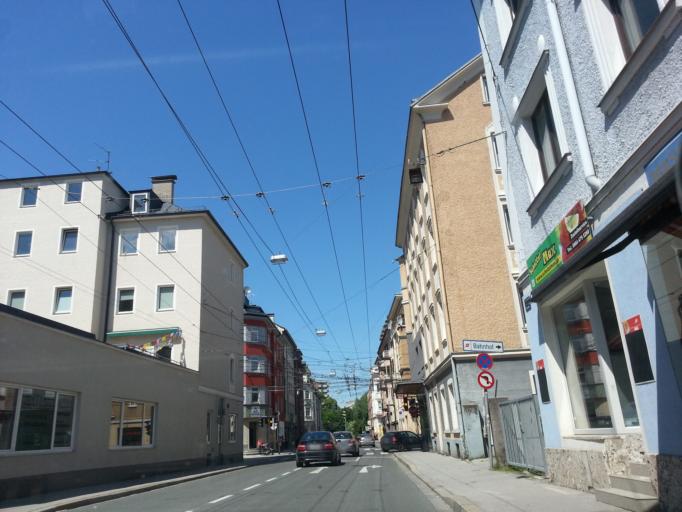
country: AT
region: Salzburg
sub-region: Salzburg Stadt
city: Salzburg
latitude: 47.8107
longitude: 13.0330
